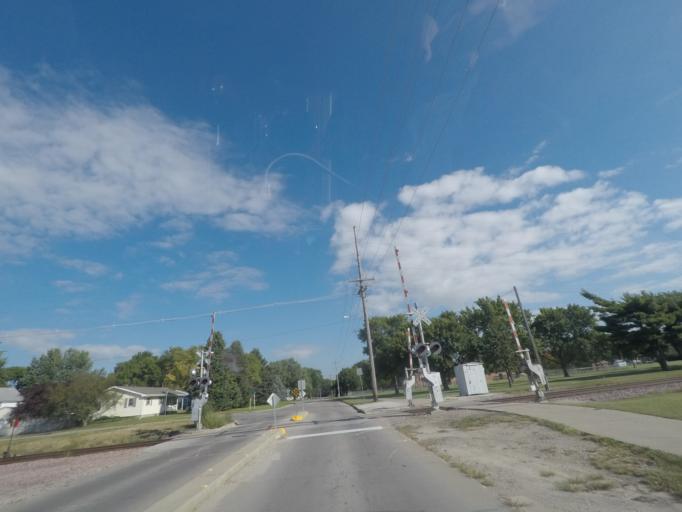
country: US
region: Iowa
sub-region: Story County
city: Nevada
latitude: 42.0152
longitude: -93.4445
